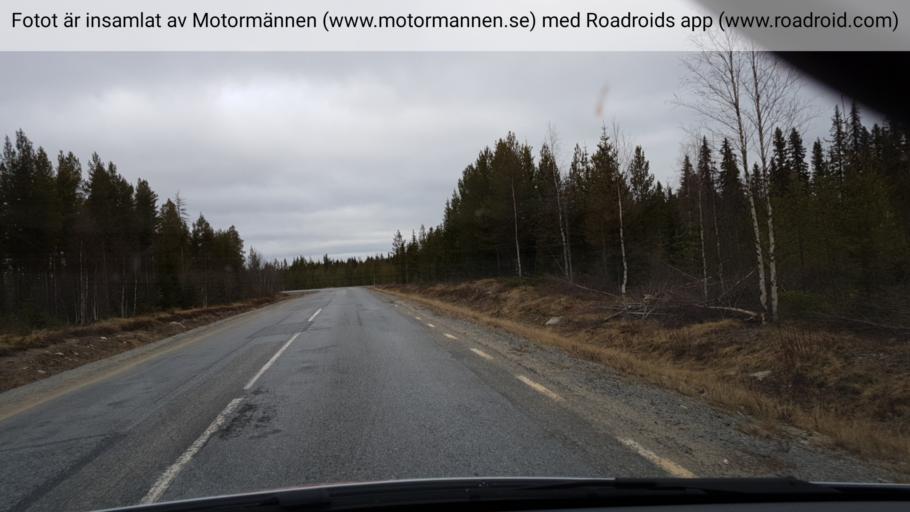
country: SE
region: Vaesterbotten
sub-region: Lycksele Kommun
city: Lycksele
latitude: 63.9757
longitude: 18.4942
